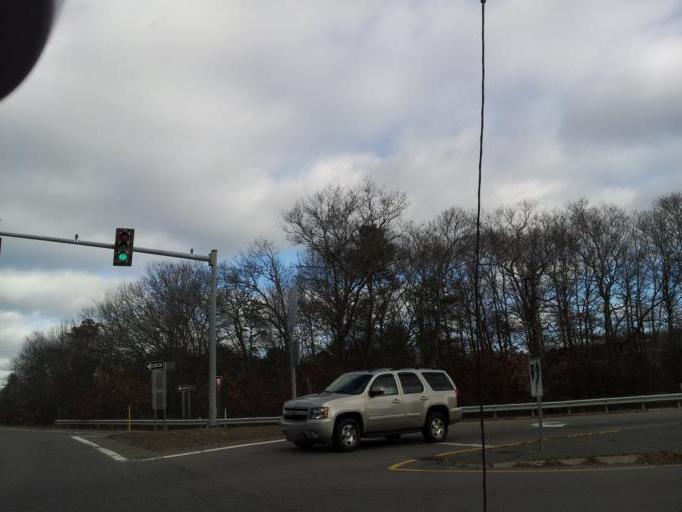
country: US
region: Massachusetts
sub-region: Plymouth County
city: Plymouth
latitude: 41.9366
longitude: -70.6563
